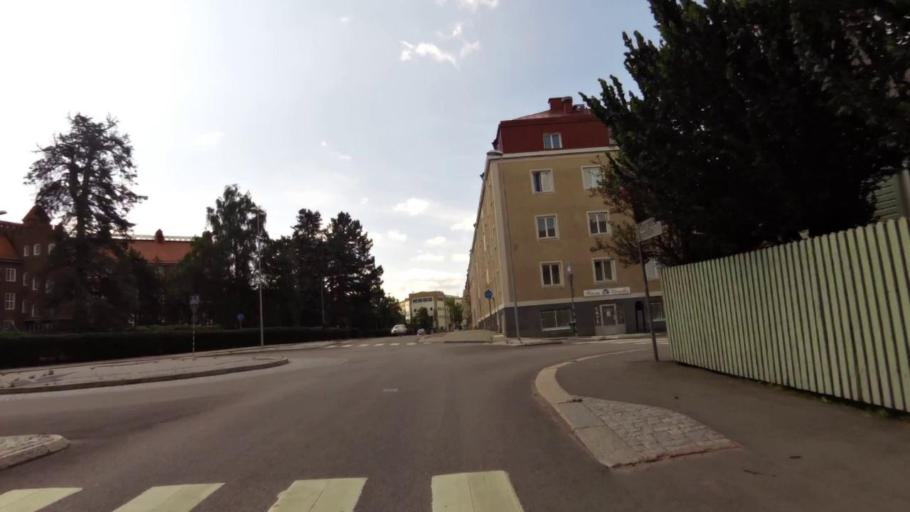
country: SE
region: OEstergoetland
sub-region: Linkopings Kommun
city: Linkoping
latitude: 58.4163
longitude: 15.6146
